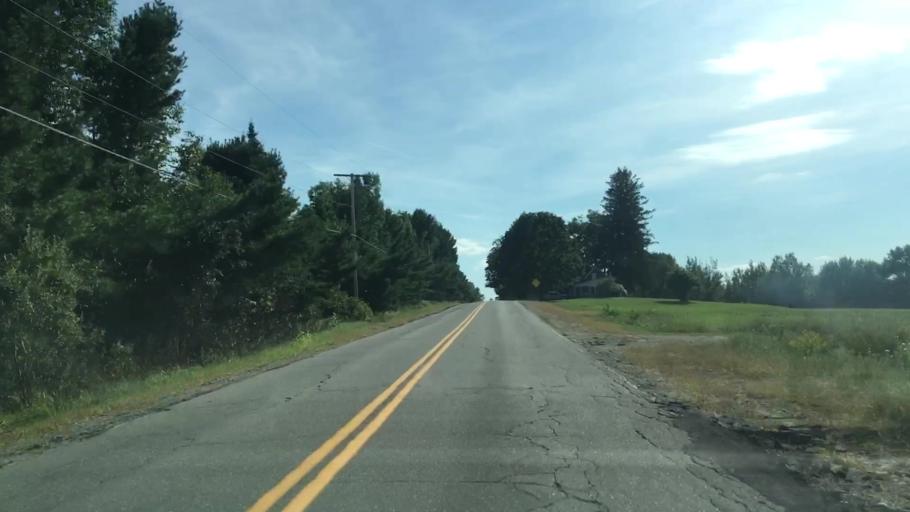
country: US
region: Maine
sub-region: Penobscot County
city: Lincoln
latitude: 45.3201
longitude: -68.5342
